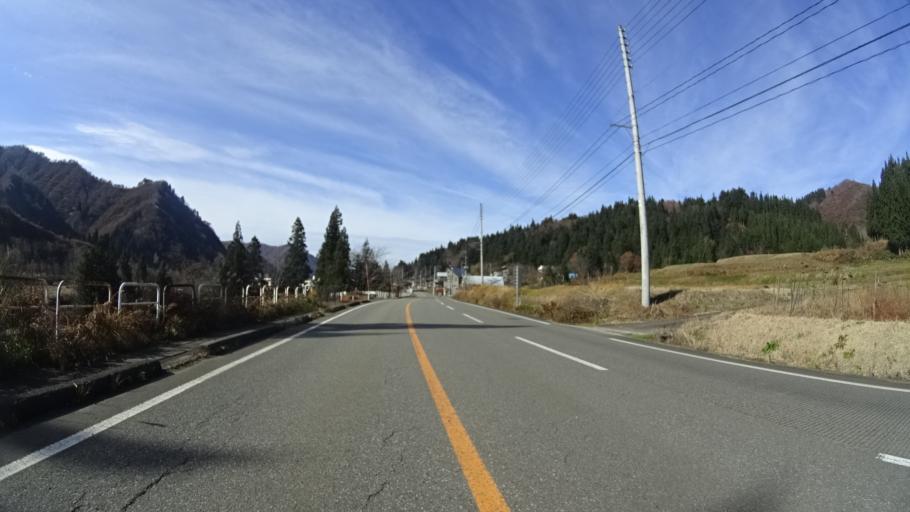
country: JP
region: Niigata
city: Muikamachi
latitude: 37.2058
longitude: 139.0684
